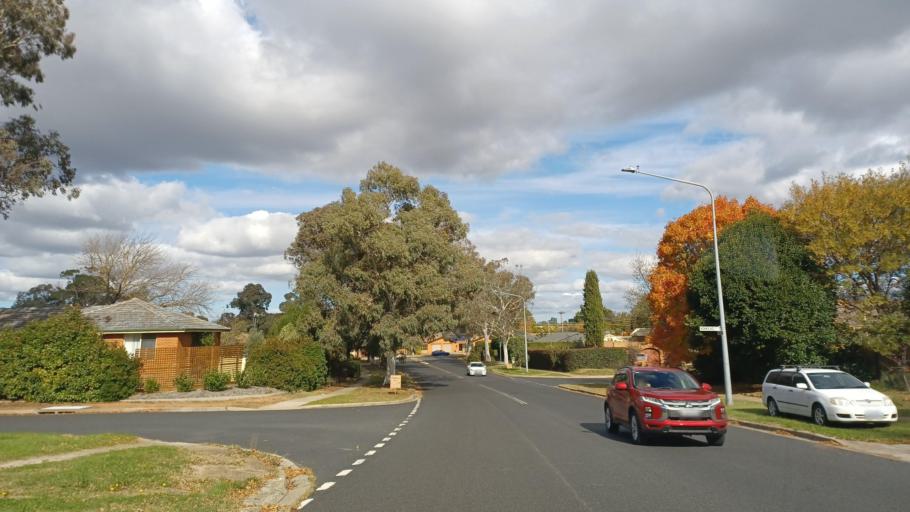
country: AU
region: Australian Capital Territory
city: Belconnen
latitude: -35.2114
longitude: 149.0741
